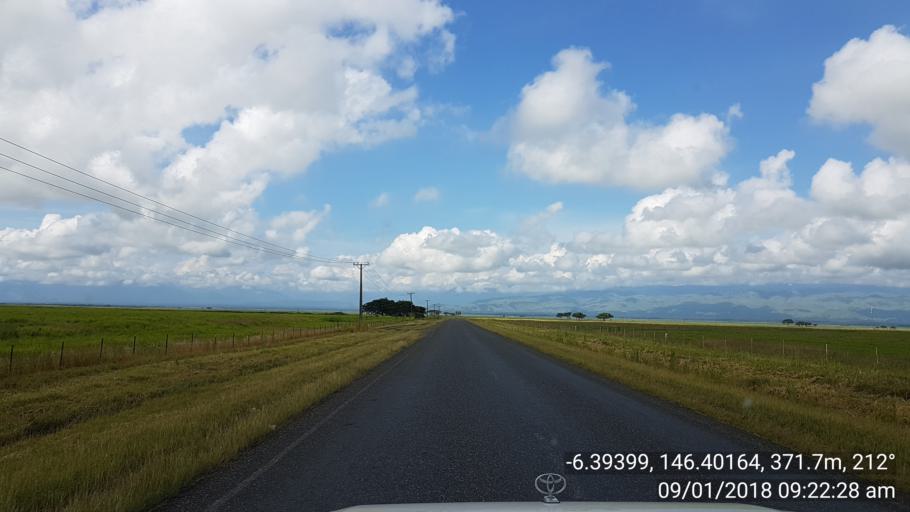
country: PG
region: Eastern Highlands
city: Kainantu
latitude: -6.3939
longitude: 146.4017
